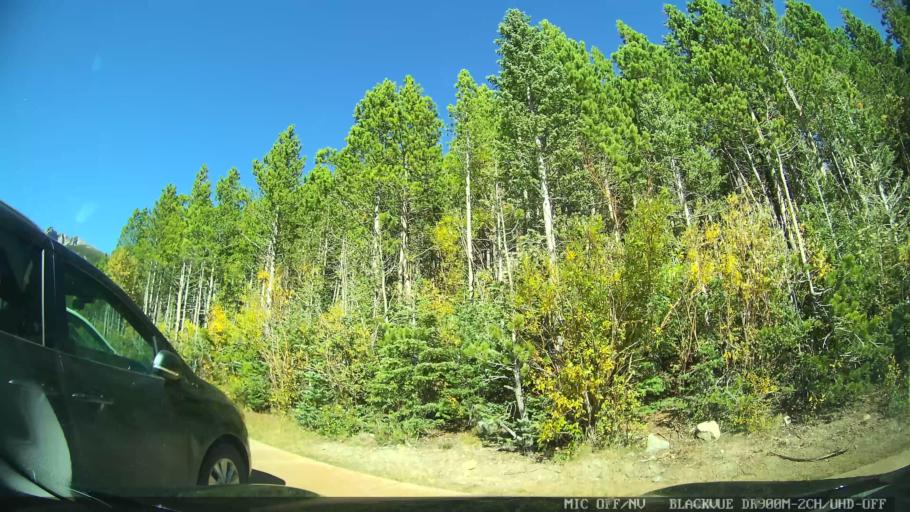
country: US
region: Colorado
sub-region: Larimer County
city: Estes Park
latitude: 40.3119
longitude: -105.6435
